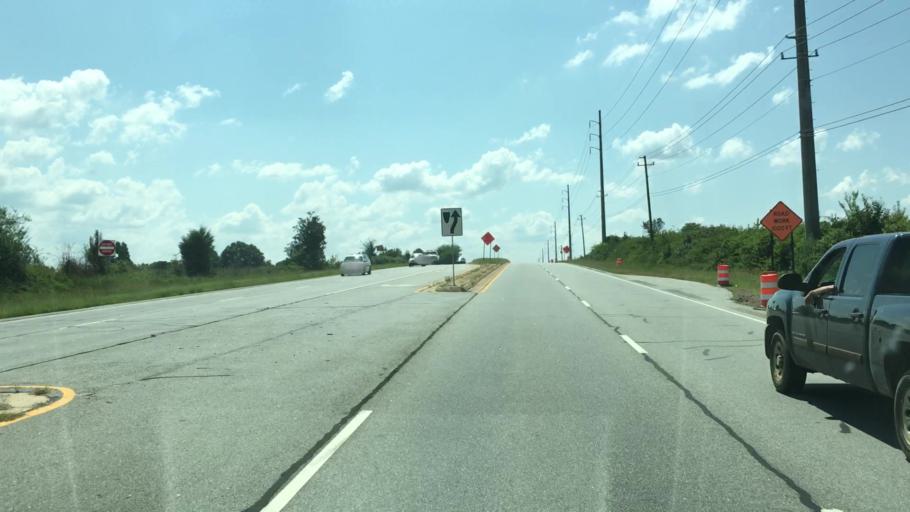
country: US
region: Georgia
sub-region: Morgan County
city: Madison
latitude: 33.5700
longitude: -83.4667
